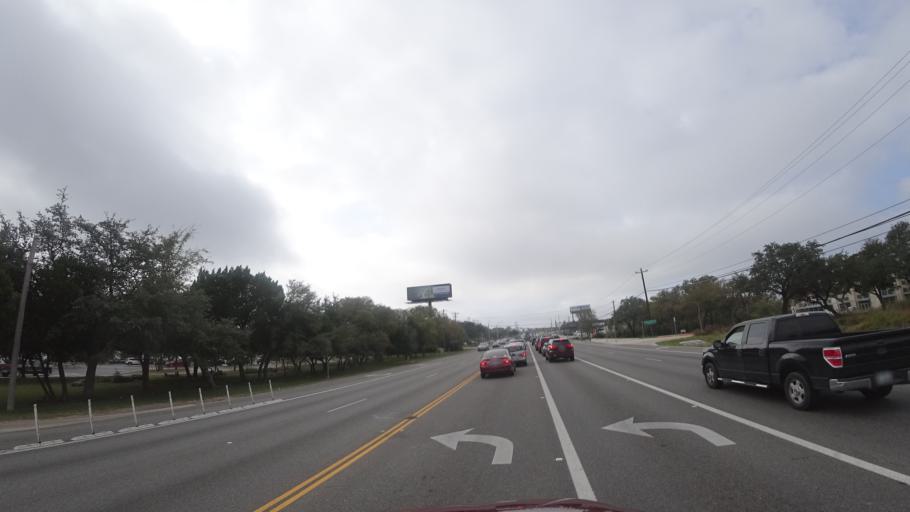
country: US
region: Texas
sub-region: Williamson County
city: Anderson Mill
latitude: 30.4053
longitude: -97.8532
